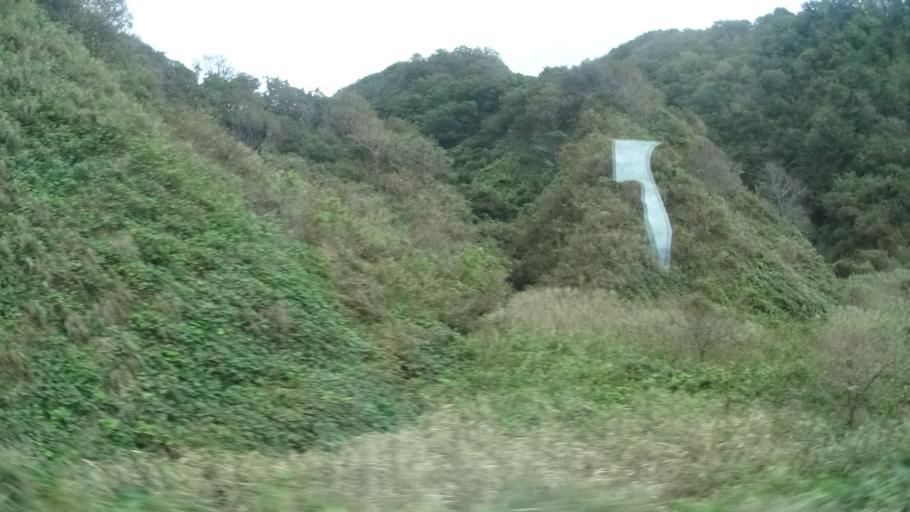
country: JP
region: Niigata
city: Murakami
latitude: 38.3954
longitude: 139.4591
